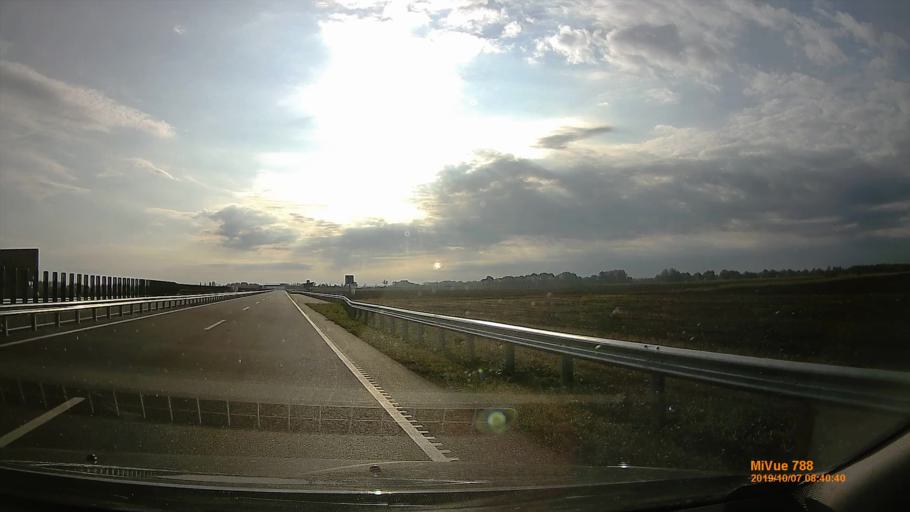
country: HU
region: Bekes
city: Bekesszentandras
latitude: 46.8228
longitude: 20.5014
